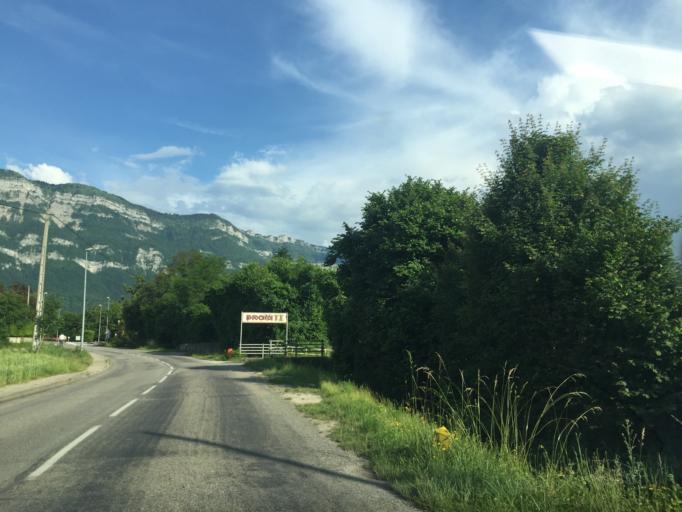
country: FR
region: Rhone-Alpes
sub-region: Departement de la Savoie
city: Drumettaz-Clarafond
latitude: 45.6620
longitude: 5.9131
